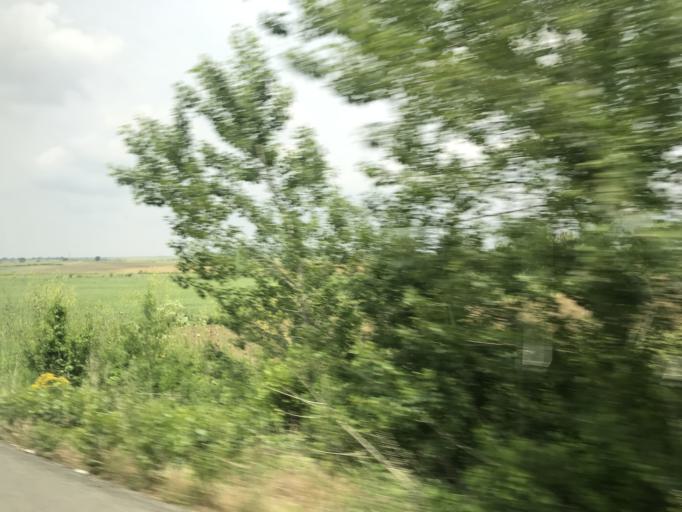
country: TR
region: Tekirdag
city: Inecik
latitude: 40.9320
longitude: 27.2200
